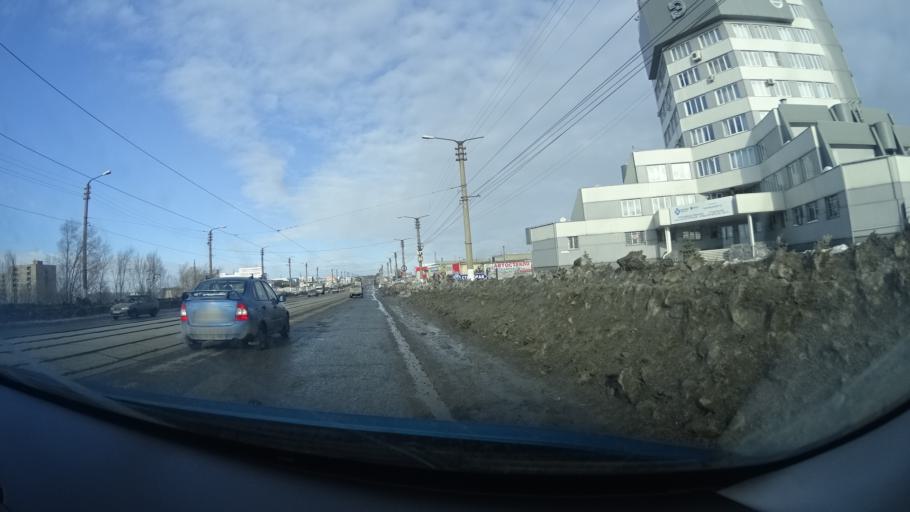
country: RU
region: Chelyabinsk
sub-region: Gorod Magnitogorsk
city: Magnitogorsk
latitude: 53.4373
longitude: 58.9945
